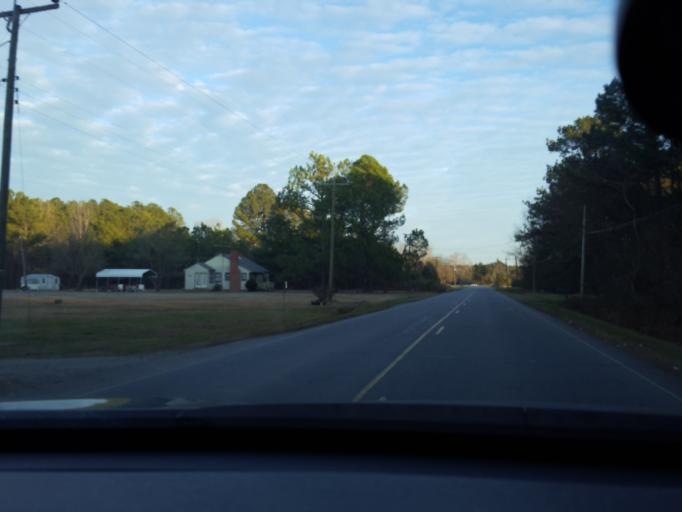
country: US
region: North Carolina
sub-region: Northampton County
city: Jackson
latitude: 36.2698
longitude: -77.2475
